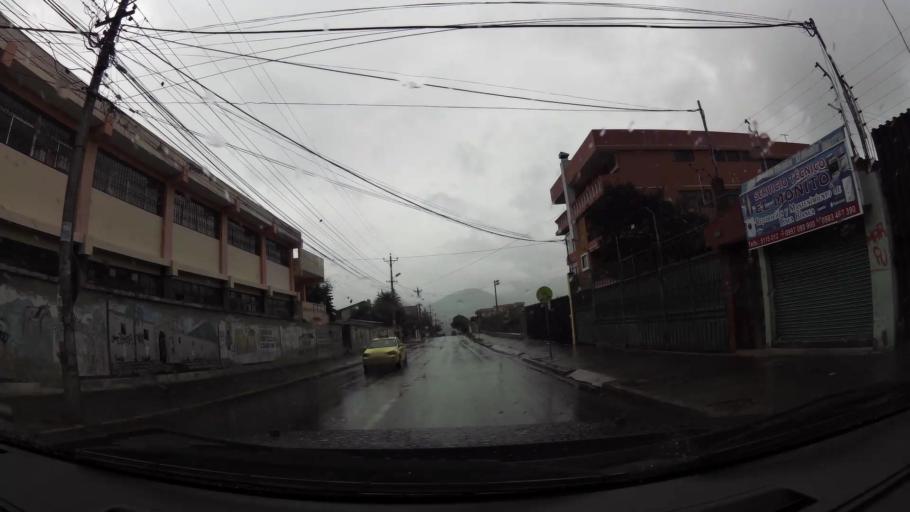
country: EC
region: Pichincha
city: Quito
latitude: -0.1119
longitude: -78.4979
